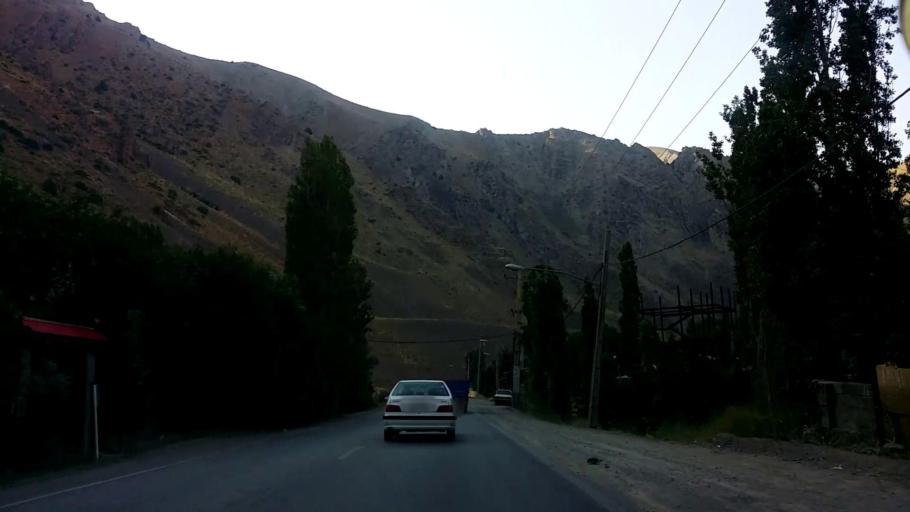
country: IR
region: Tehran
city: Tajrish
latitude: 36.0377
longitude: 51.3111
